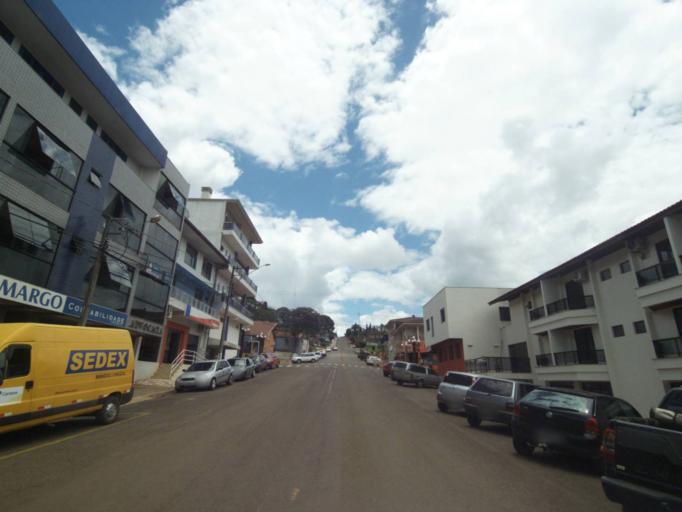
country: BR
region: Parana
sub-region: Uniao Da Vitoria
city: Uniao da Vitoria
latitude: -26.1586
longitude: -51.5543
